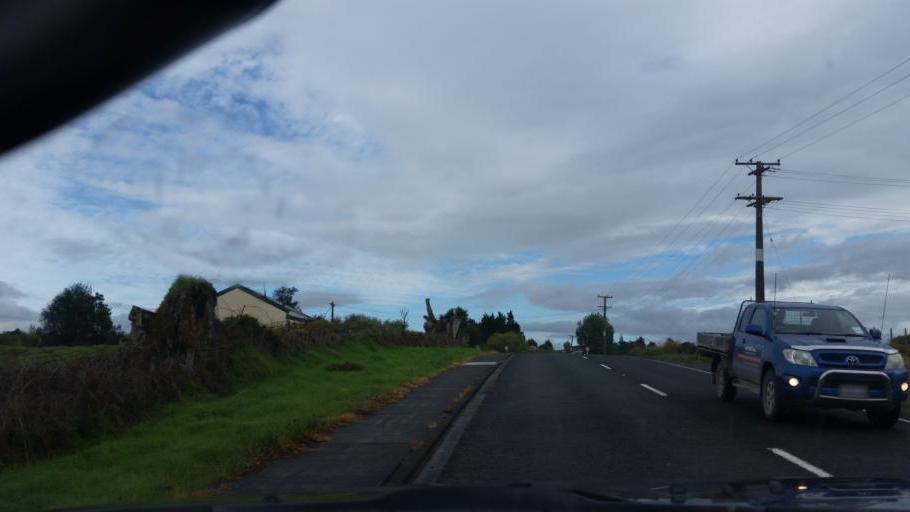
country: NZ
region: Northland
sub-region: Whangarei
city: Ruakaka
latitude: -36.1126
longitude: 174.3642
